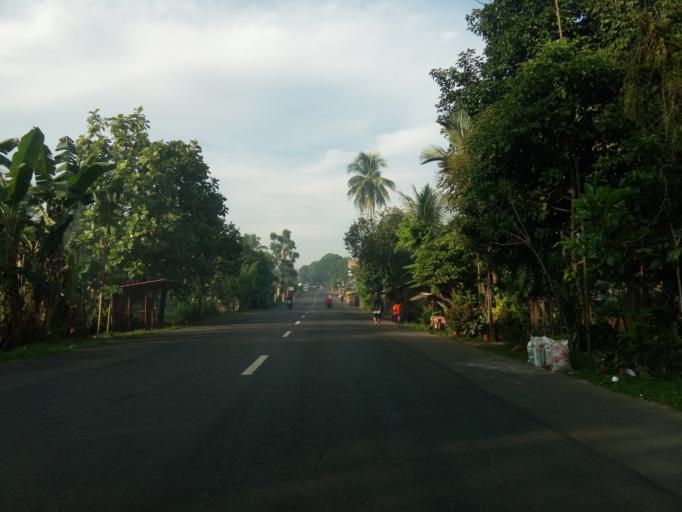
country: PH
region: Caraga
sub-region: Province of Surigao del Norte
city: Tubod
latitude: 9.5589
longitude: 125.5695
